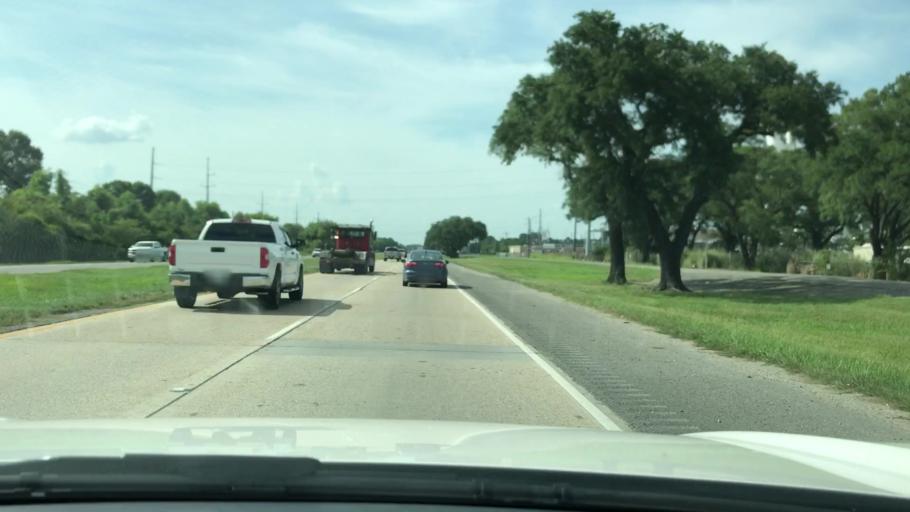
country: US
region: Louisiana
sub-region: West Baton Rouge Parish
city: Addis
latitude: 30.3213
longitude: -91.2519
